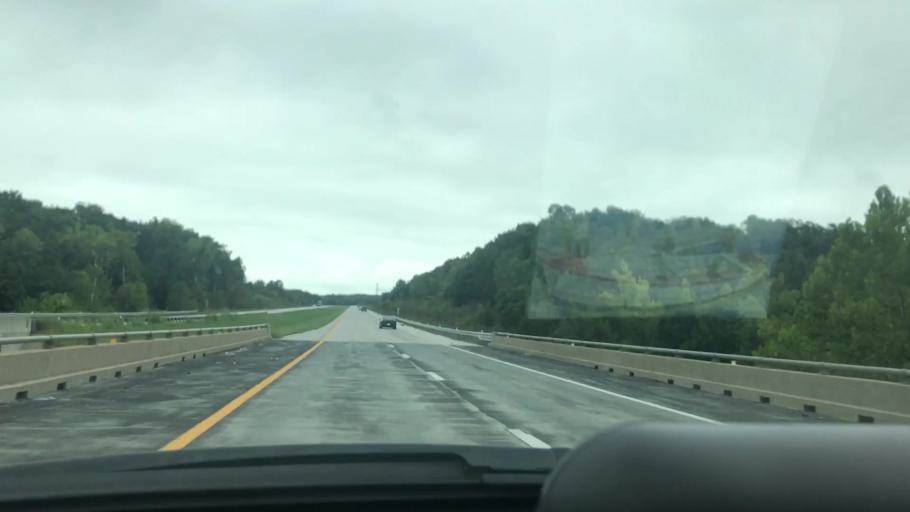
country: US
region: Missouri
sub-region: Greene County
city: Strafford
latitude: 37.3101
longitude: -93.1728
